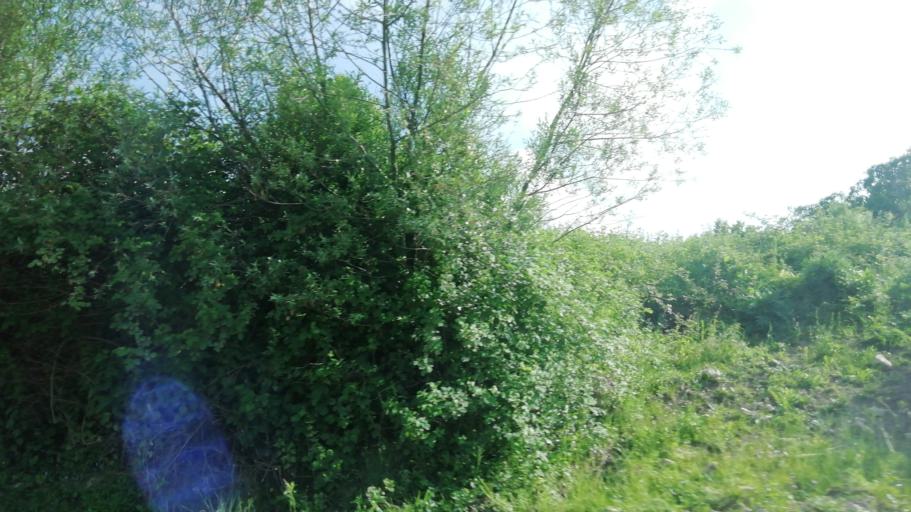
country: TR
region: Karabuk
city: Eskipazar
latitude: 41.0801
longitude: 32.5593
